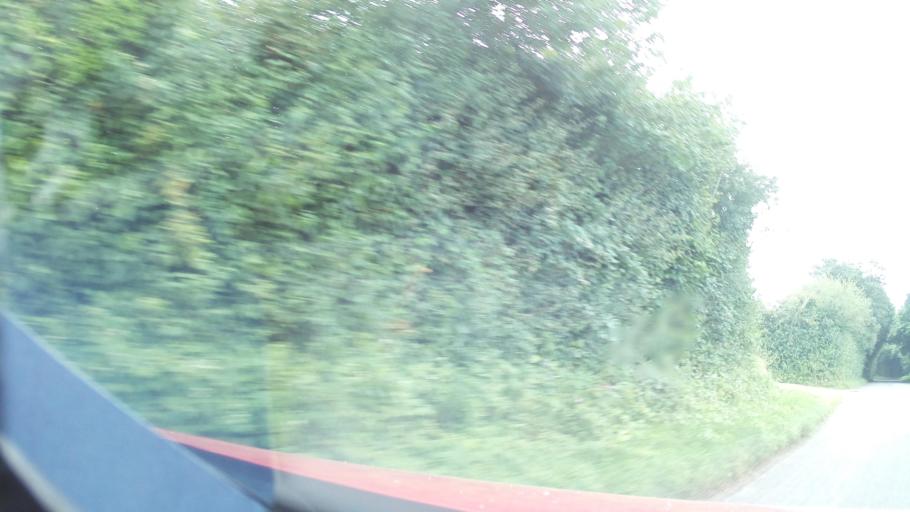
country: GB
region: England
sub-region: Somerset
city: Evercreech
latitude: 51.1790
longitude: -2.5079
